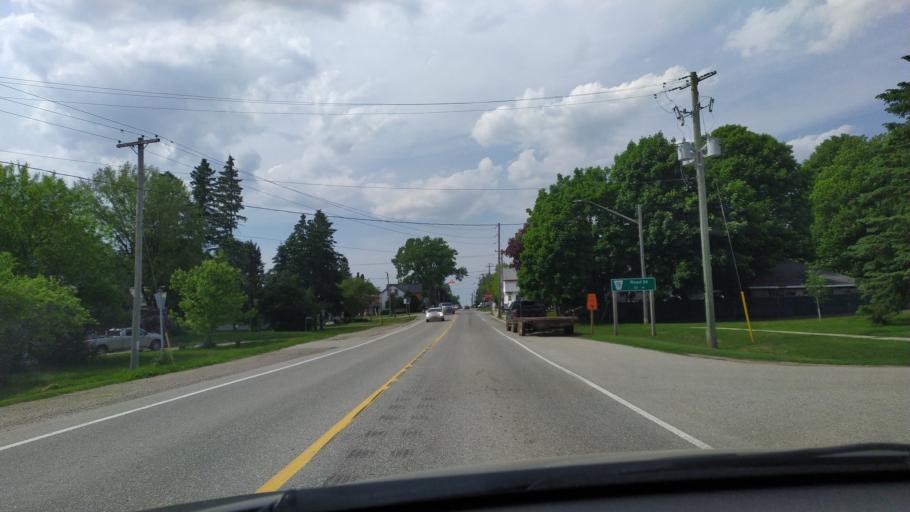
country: CA
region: Ontario
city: Dorchester
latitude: 43.1379
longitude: -81.0296
